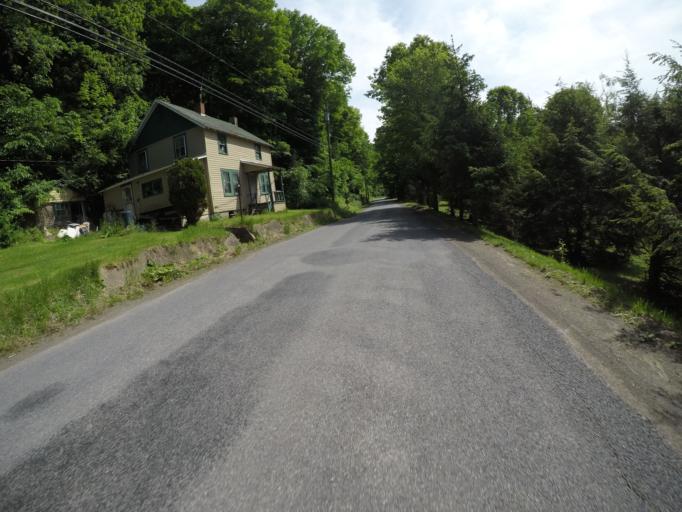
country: US
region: New York
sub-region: Delaware County
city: Stamford
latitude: 42.1397
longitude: -74.6500
